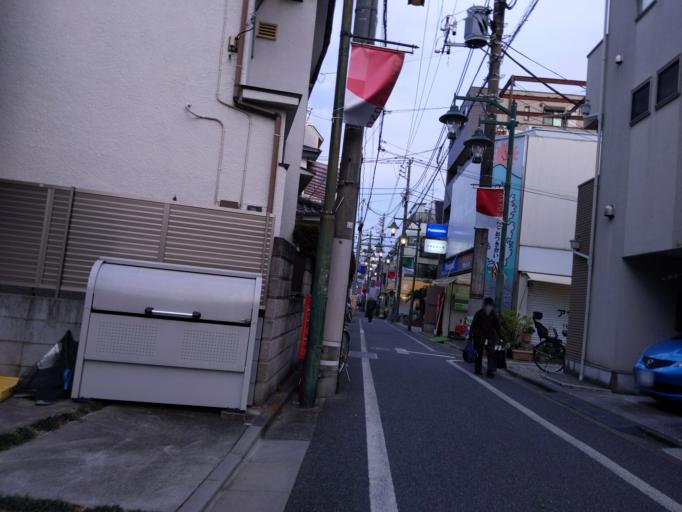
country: JP
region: Tokyo
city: Tokyo
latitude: 35.6170
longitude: 139.6951
